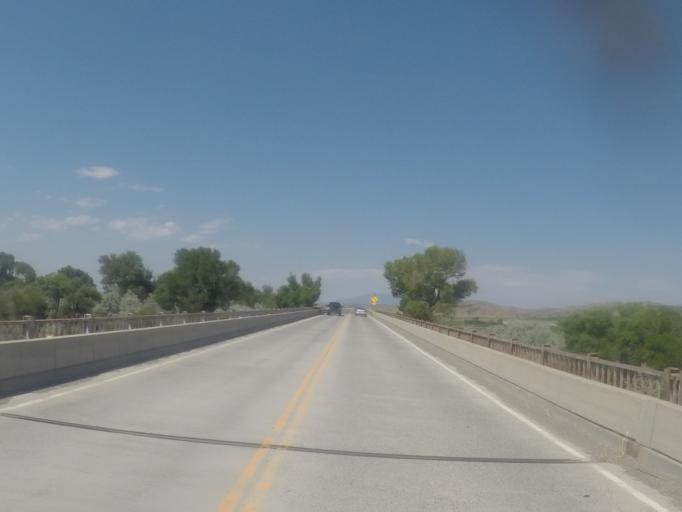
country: US
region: Montana
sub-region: Broadwater County
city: Townsend
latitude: 46.1739
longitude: -111.4458
